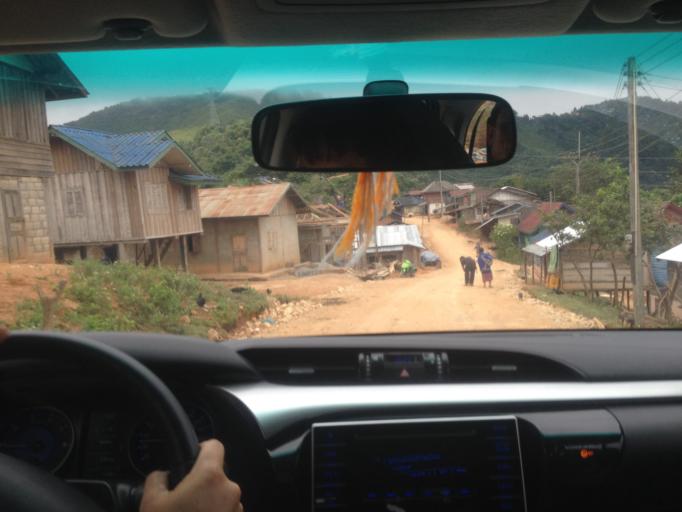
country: TH
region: Nan
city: Chaloem Phra Kiat
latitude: 19.9996
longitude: 101.1279
